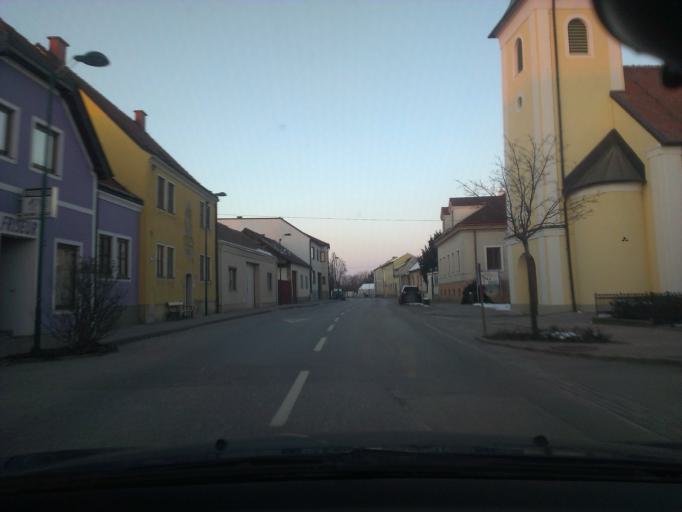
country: AT
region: Lower Austria
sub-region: Politischer Bezirk Bruck an der Leitha
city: Gotzendorf an der Leitha
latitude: 48.0133
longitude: 16.5796
